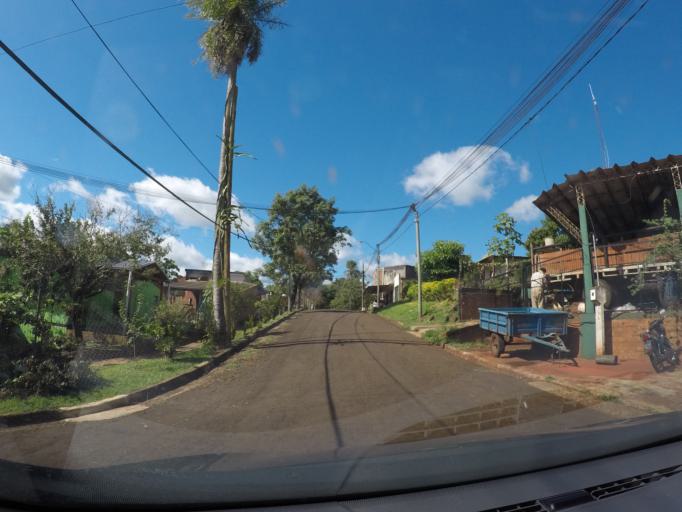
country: AR
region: Misiones
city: Puerto Rico
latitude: -26.8002
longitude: -55.0259
